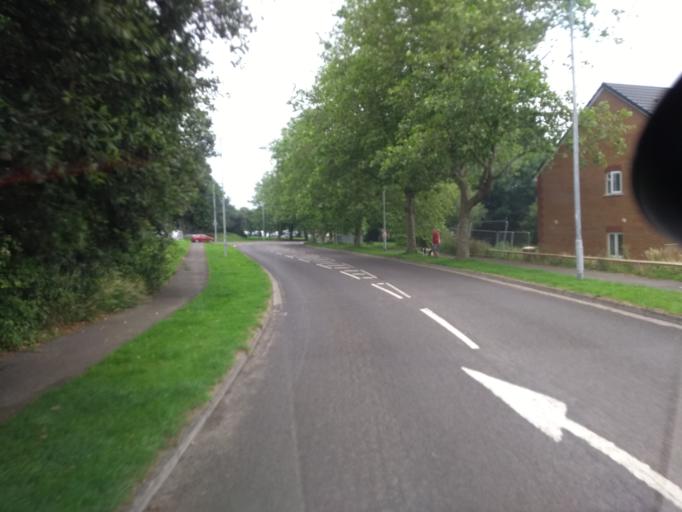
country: GB
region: England
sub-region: Somerset
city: Chard
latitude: 50.8838
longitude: -2.9565
